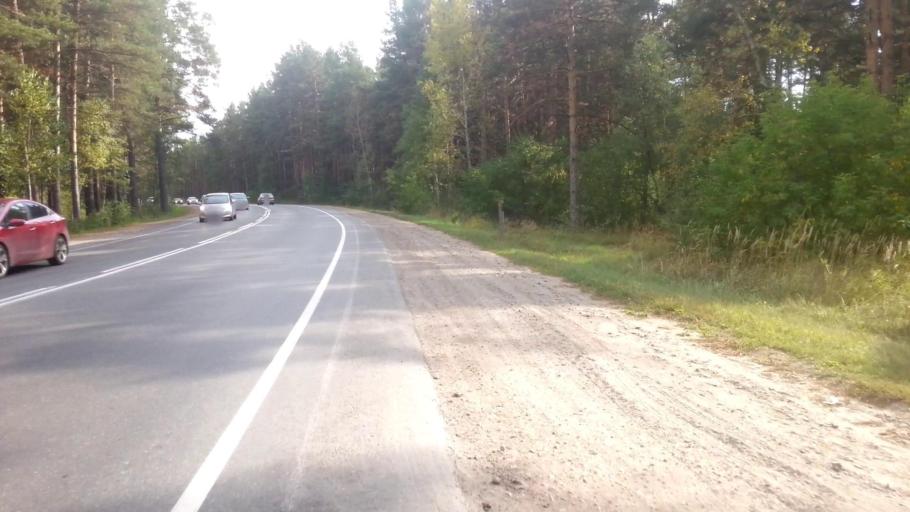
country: RU
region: Altai Krai
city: Yuzhnyy
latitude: 53.2988
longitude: 83.7028
